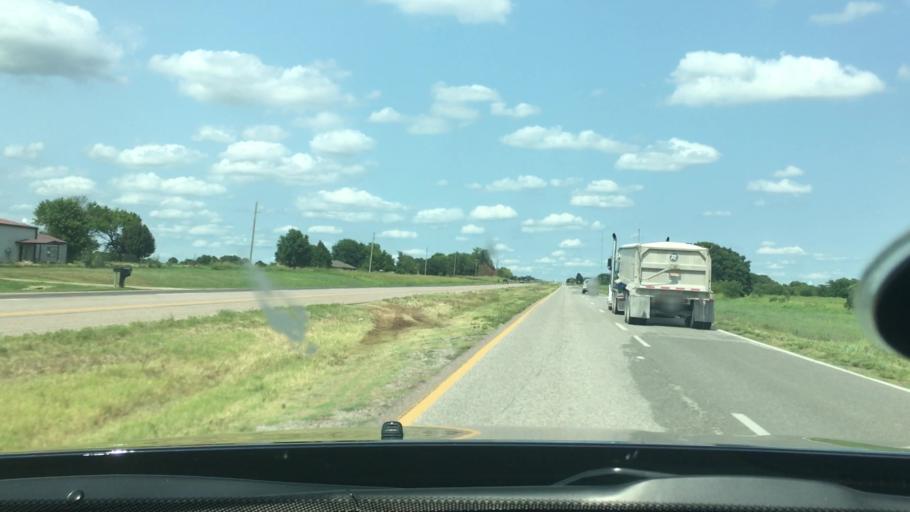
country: US
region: Oklahoma
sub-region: Pontotoc County
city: Ada
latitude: 34.6716
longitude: -96.7799
